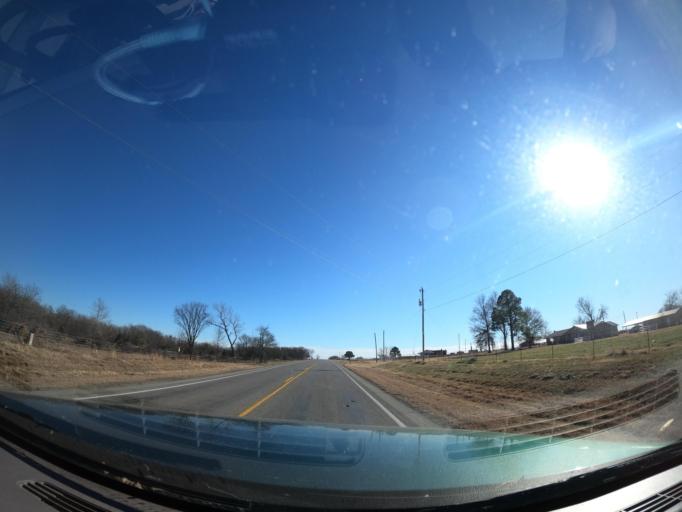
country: US
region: Oklahoma
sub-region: Muskogee County
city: Haskell
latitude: 35.7647
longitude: -95.6495
